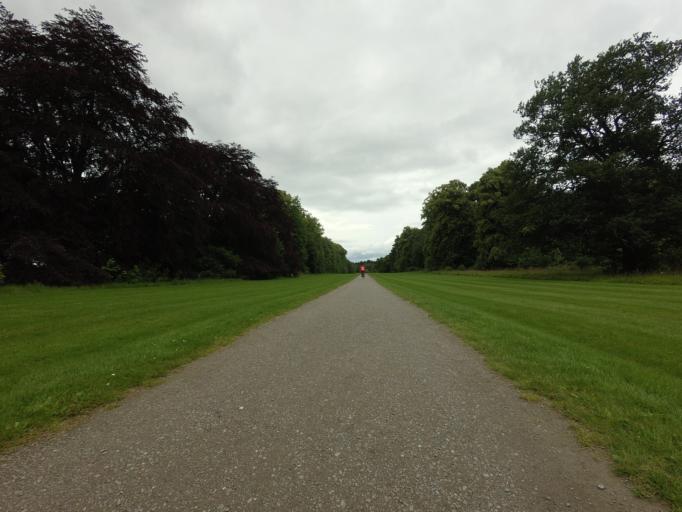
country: GB
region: Scotland
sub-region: Moray
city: Forres
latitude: 57.5975
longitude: -3.7107
